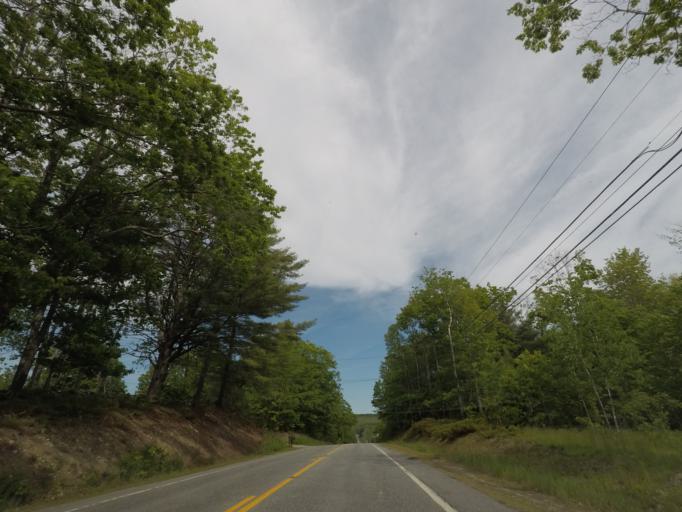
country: US
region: Maine
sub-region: Sagadahoc County
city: Richmond
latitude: 44.0860
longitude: -69.7606
